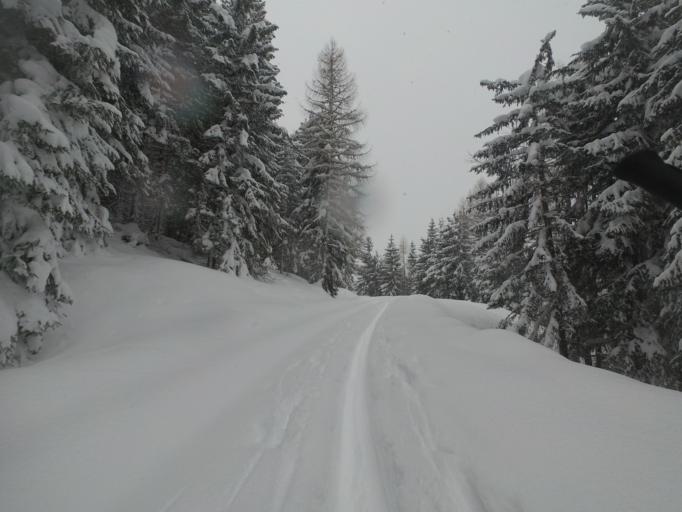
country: AT
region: Salzburg
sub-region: Politischer Bezirk Sankt Johann im Pongau
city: Sankt Johann im Pongau
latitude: 47.3131
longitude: 13.2134
